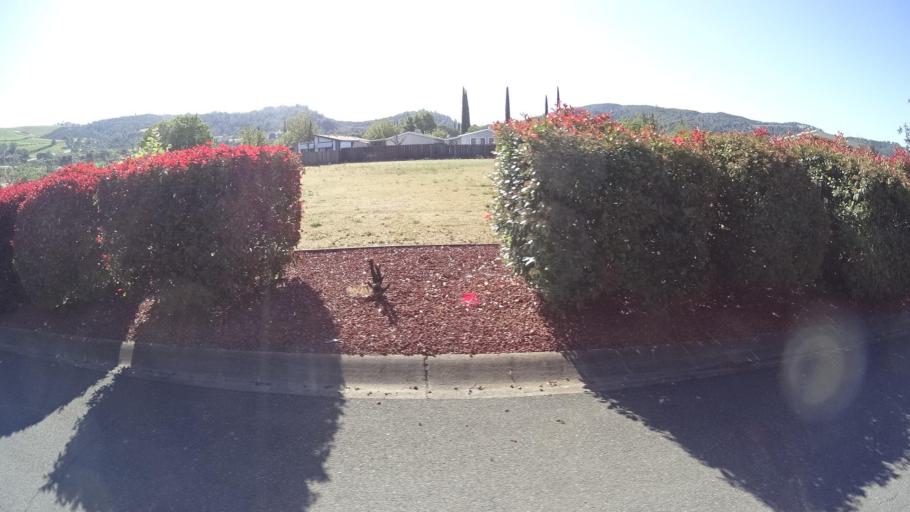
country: US
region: California
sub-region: Lake County
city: Clearlake Oaks
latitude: 39.0207
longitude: -122.6522
